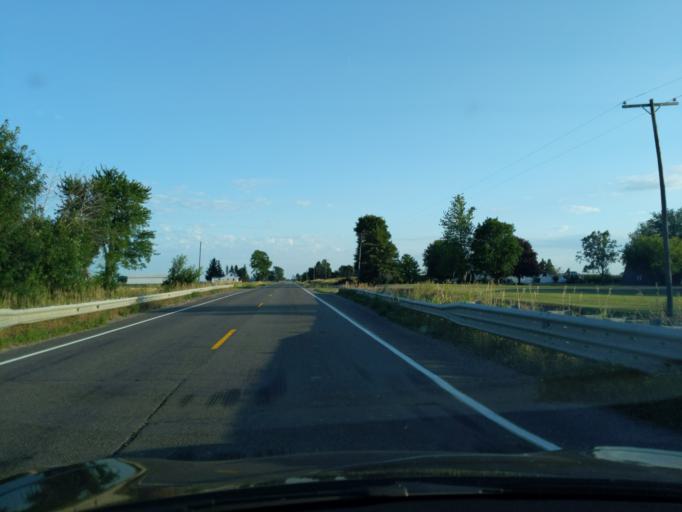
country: US
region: Michigan
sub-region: Gratiot County
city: Breckenridge
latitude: 43.5078
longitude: -84.3698
